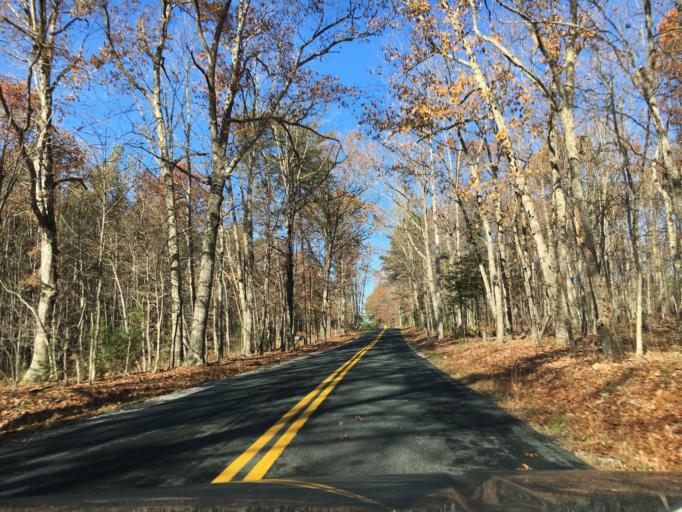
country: US
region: Virginia
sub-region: Buckingham County
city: Buckingham
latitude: 37.4524
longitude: -78.6785
